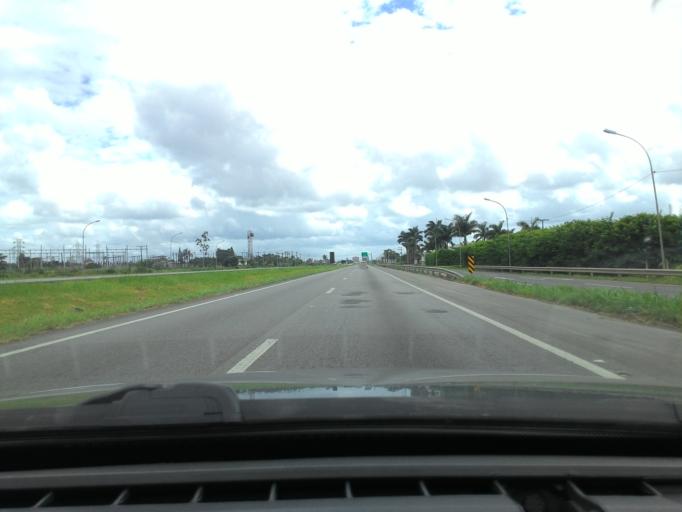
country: BR
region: Sao Paulo
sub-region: Registro
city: Registro
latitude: -24.5256
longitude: -47.8550
